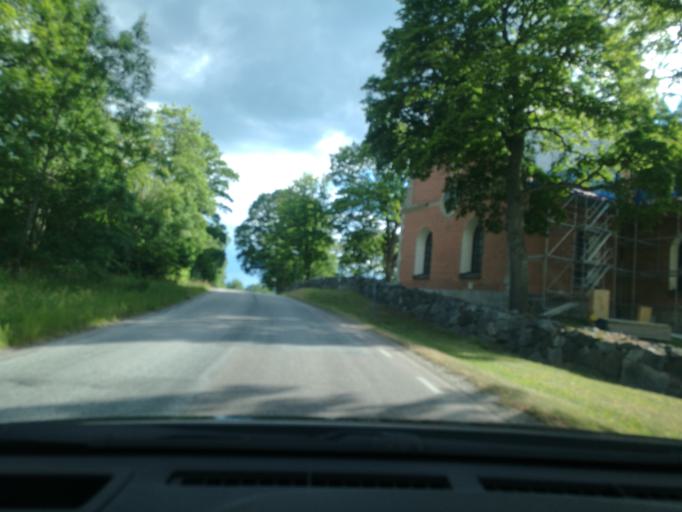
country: SE
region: Soedermanland
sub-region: Eskilstuna Kommun
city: Arla
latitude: 59.4100
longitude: 16.6918
